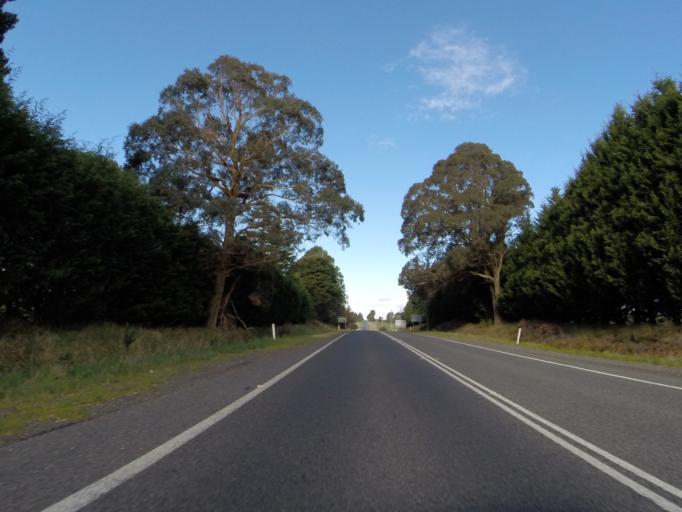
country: AU
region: New South Wales
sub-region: Wingecarribee
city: Moss Vale
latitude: -34.5654
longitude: 150.4126
